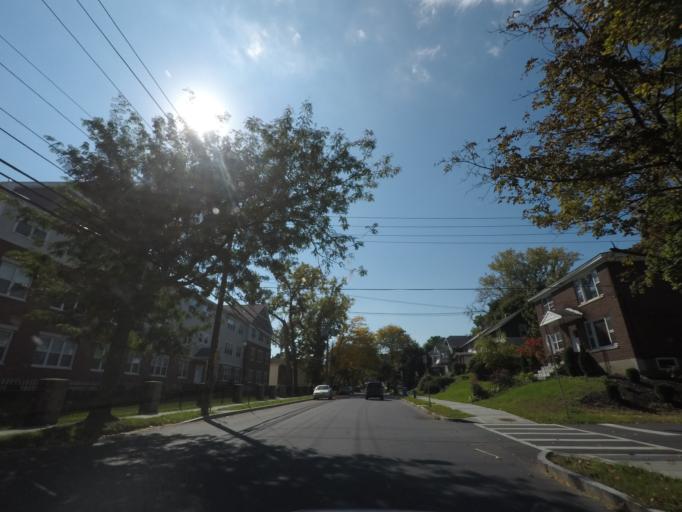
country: US
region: New York
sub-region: Albany County
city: West Albany
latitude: 42.6594
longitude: -73.7996
